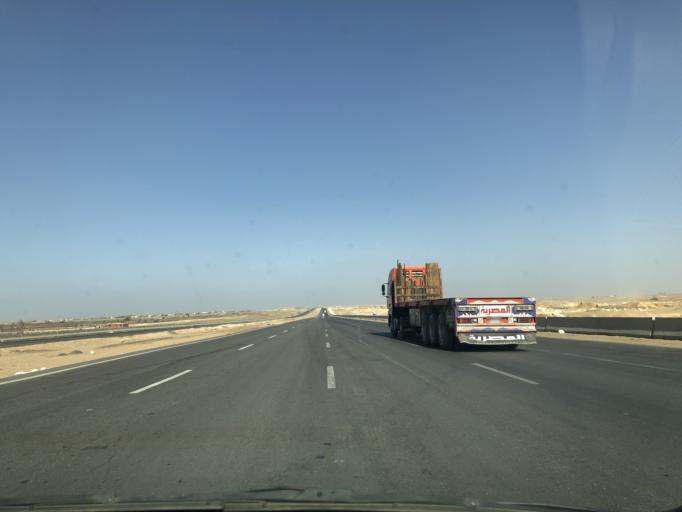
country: EG
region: Muhafazat al Minufiyah
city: Ashmun
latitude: 30.0674
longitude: 30.8501
